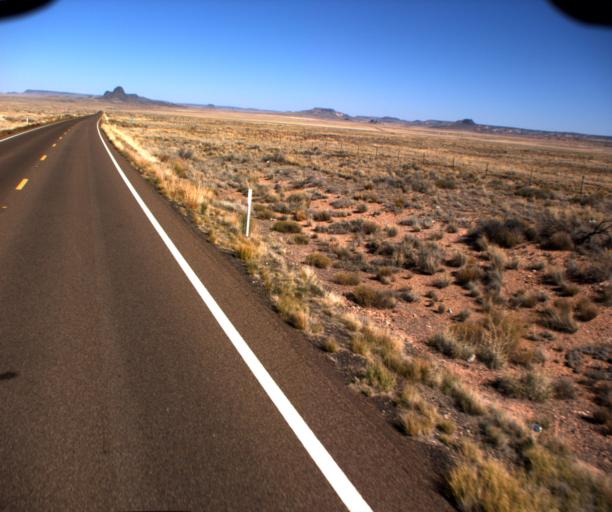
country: US
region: Arizona
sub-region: Navajo County
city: Dilkon
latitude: 35.2151
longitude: -110.4372
